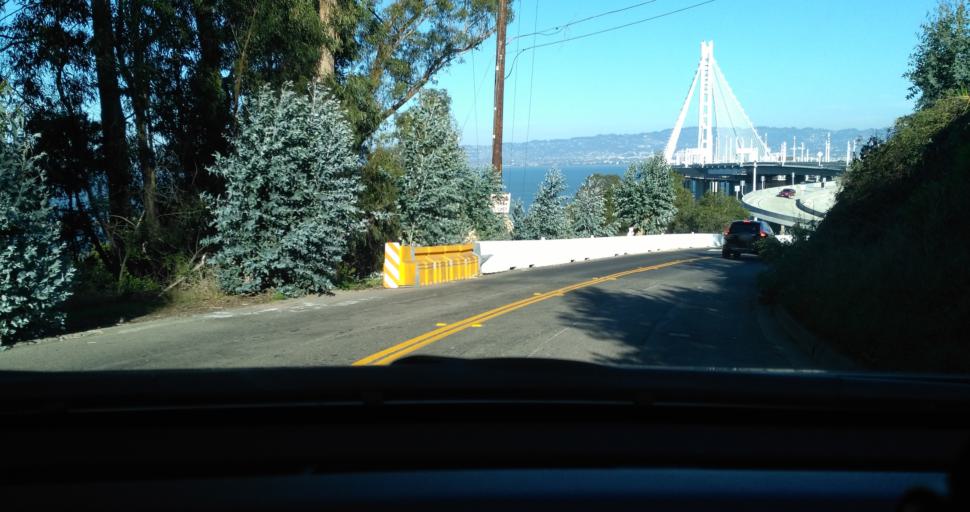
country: US
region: California
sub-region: San Francisco County
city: San Francisco
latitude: 37.8117
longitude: -122.3658
